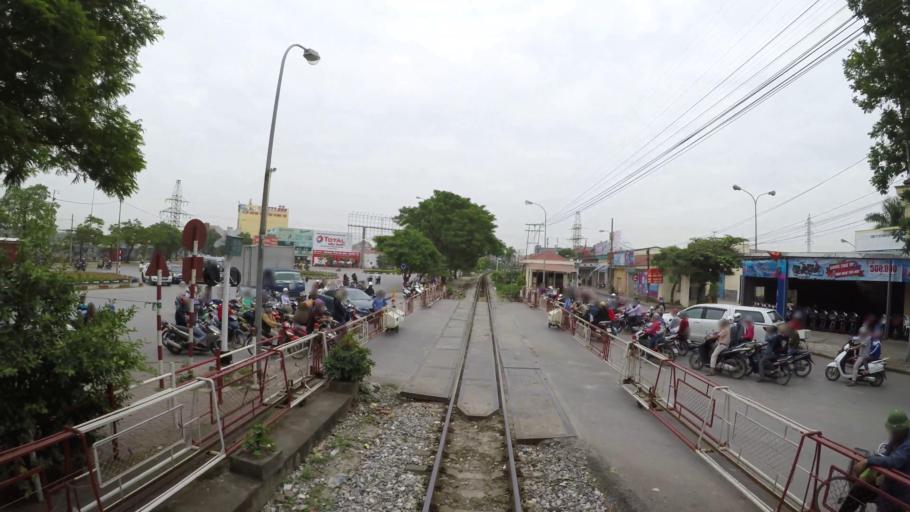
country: VN
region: Hai Phong
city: An Duong
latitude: 20.8758
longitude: 106.6362
